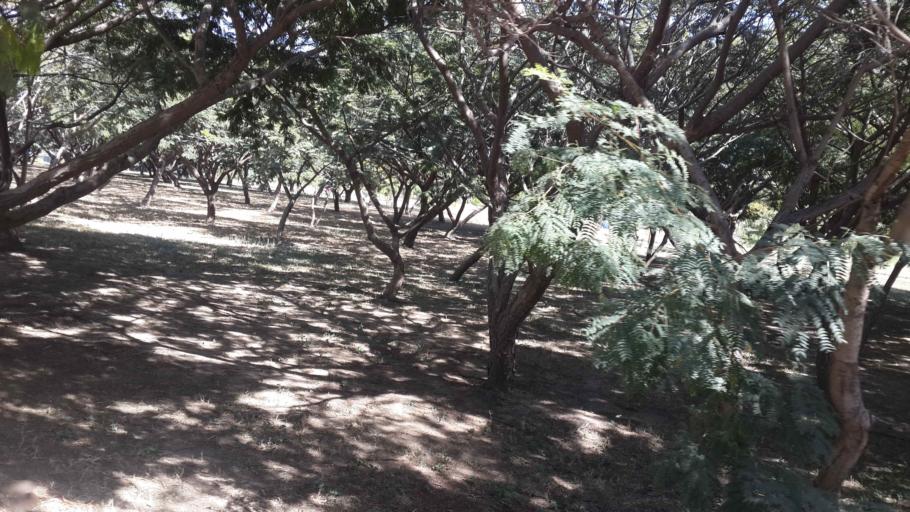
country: MX
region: Jalisco
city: Guadalajara
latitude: 20.6734
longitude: -103.4426
